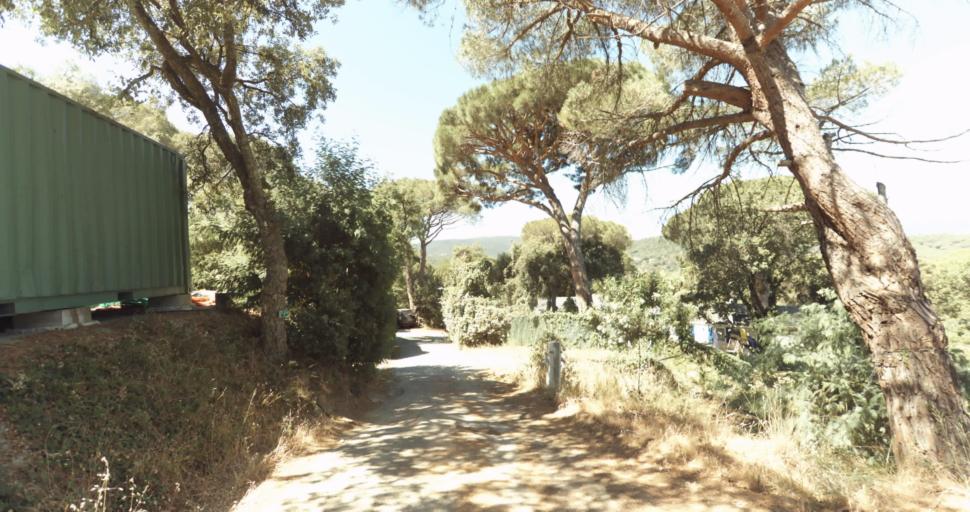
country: FR
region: Provence-Alpes-Cote d'Azur
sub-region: Departement du Var
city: Gassin
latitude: 43.2420
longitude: 6.5791
